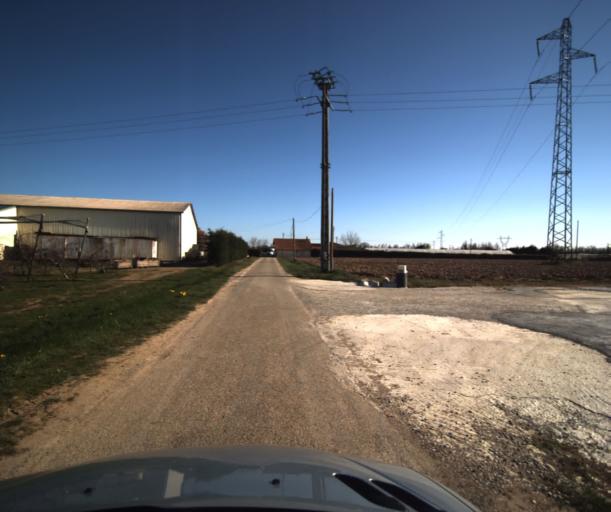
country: FR
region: Midi-Pyrenees
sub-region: Departement du Tarn-et-Garonne
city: Bressols
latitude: 43.9411
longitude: 1.3307
